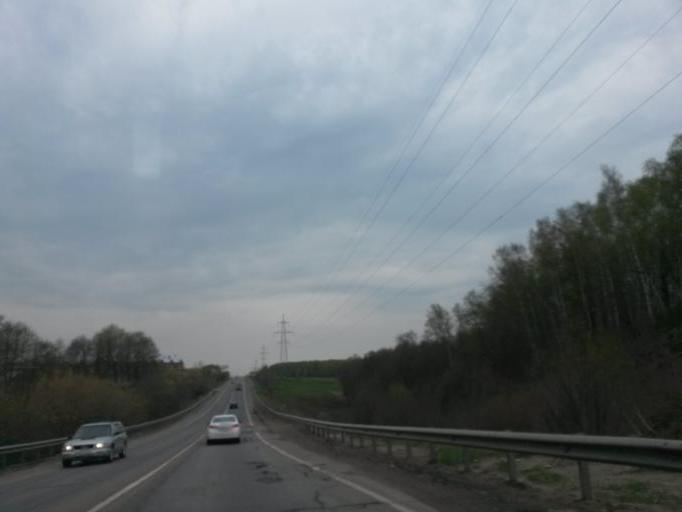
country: RU
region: Moskovskaya
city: Shcherbinka
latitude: 55.4845
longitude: 37.6069
